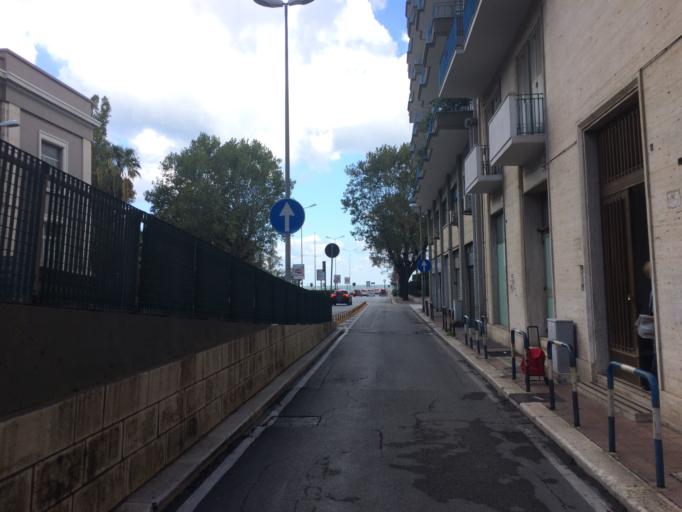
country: IT
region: Apulia
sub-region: Provincia di Bari
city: Bari
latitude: 41.1177
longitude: 16.8891
